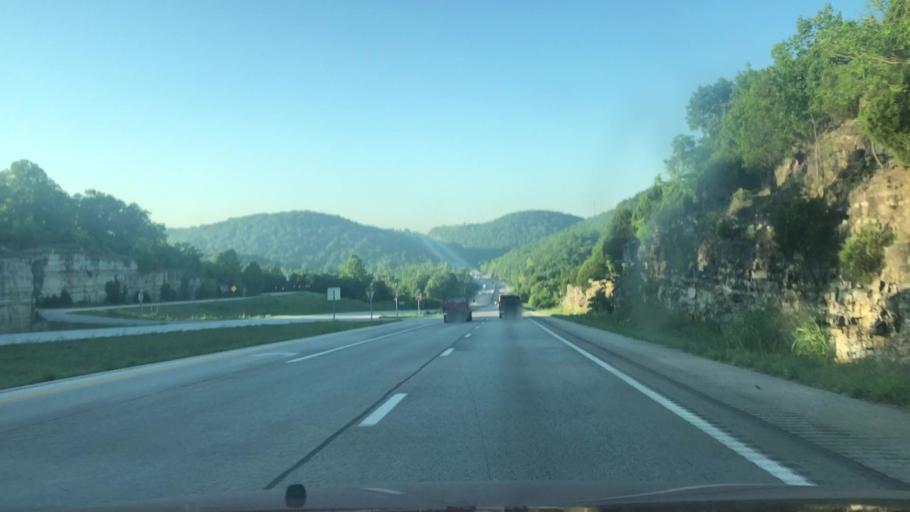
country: US
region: Missouri
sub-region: Christian County
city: Ozark
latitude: 36.8675
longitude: -93.2293
